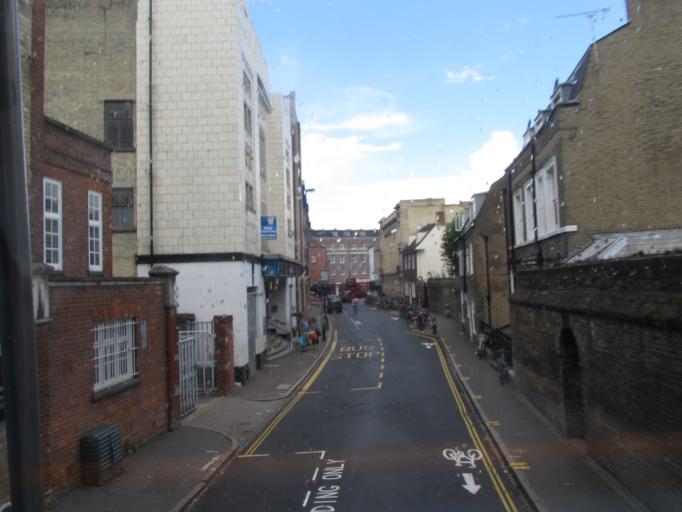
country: GB
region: England
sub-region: Cambridgeshire
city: Cambridge
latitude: 52.2060
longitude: 0.1217
